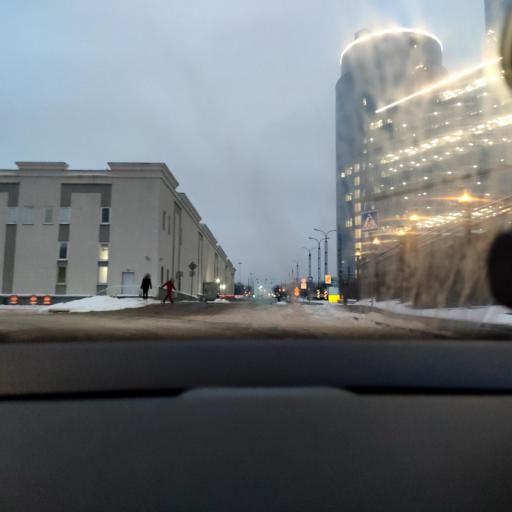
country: RU
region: Moscow
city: Strogino
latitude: 55.8184
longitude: 37.3850
